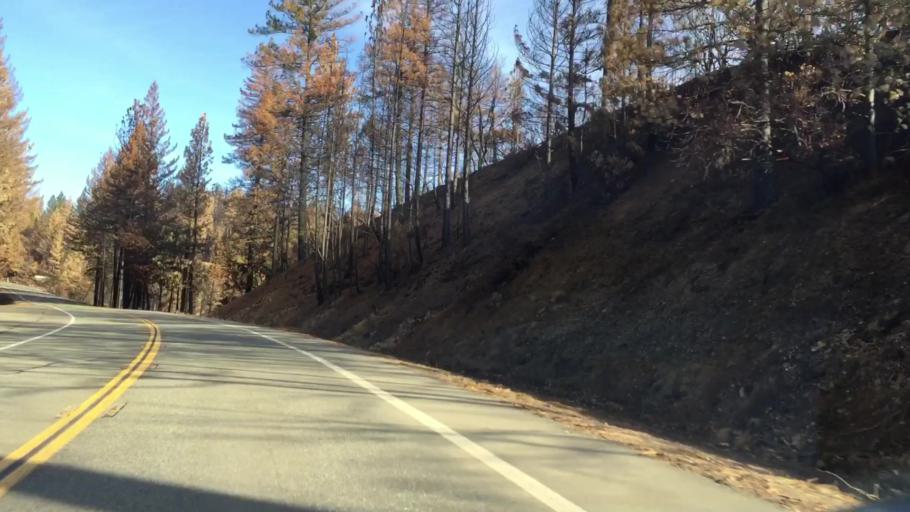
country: US
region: California
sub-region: Butte County
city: Magalia
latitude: 39.7293
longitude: -121.4942
